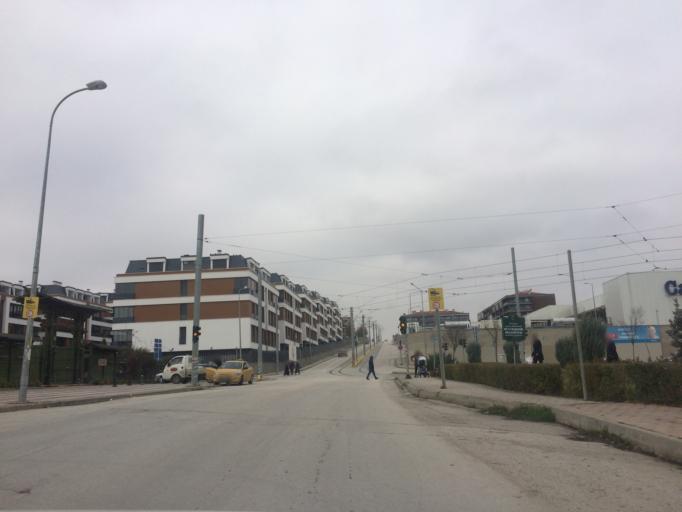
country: TR
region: Eskisehir
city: Eskisehir
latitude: 39.7787
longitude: 30.4771
